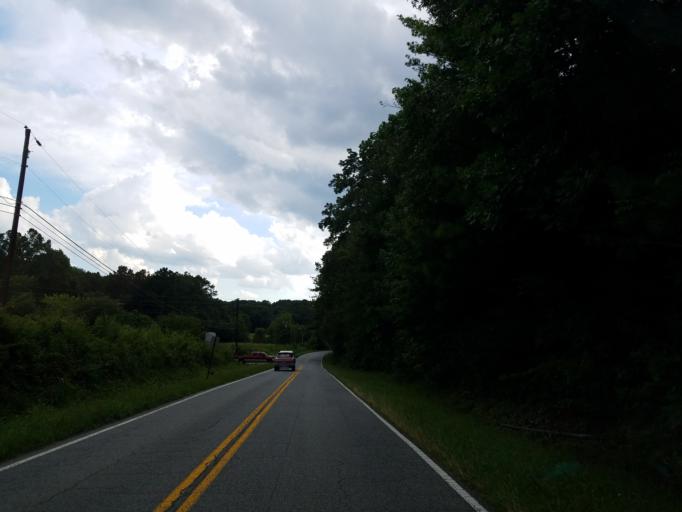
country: US
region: Georgia
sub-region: Bartow County
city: Cartersville
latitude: 34.2589
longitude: -84.8412
